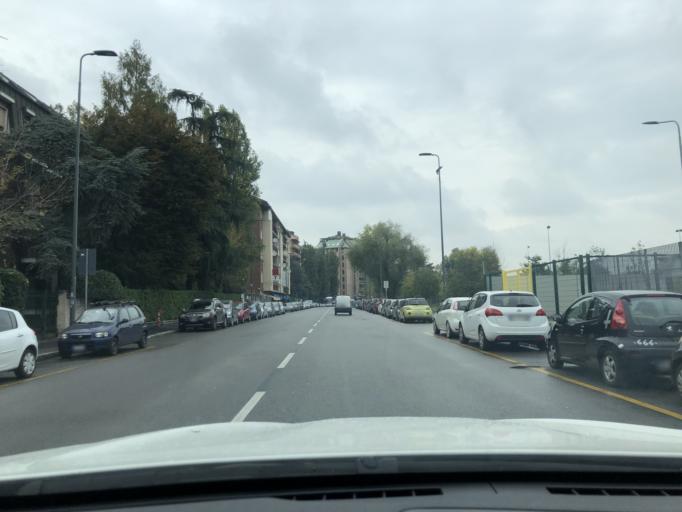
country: IT
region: Lombardy
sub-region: Citta metropolitana di Milano
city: Figino
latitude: 45.4778
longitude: 9.1174
